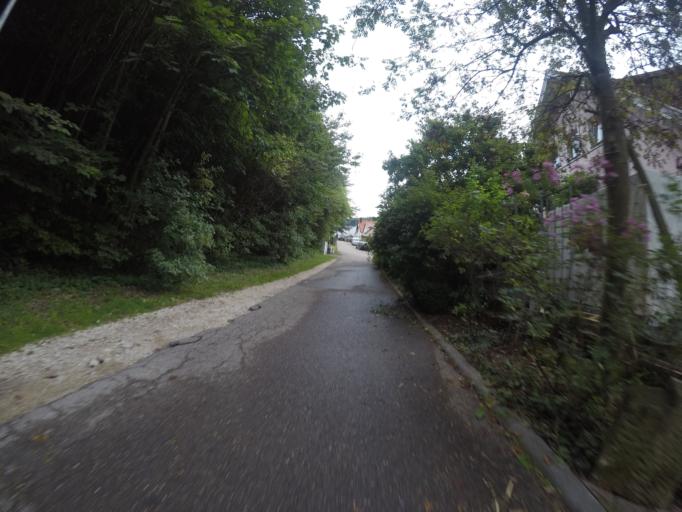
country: DE
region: Baden-Wuerttemberg
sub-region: Tuebingen Region
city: Pfullingen
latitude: 48.4141
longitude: 9.2613
